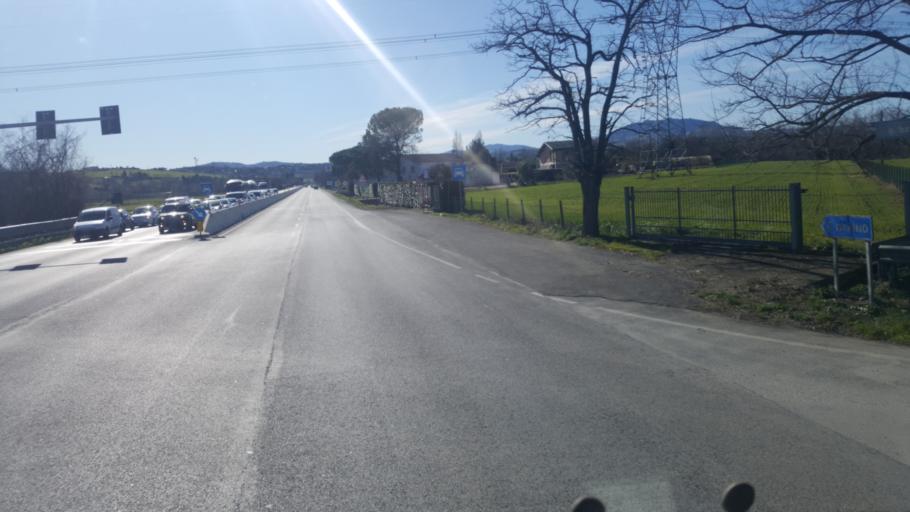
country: IT
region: Emilia-Romagna
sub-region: Provincia di Rimini
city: Cerasolo
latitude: 44.0126
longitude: 12.5464
